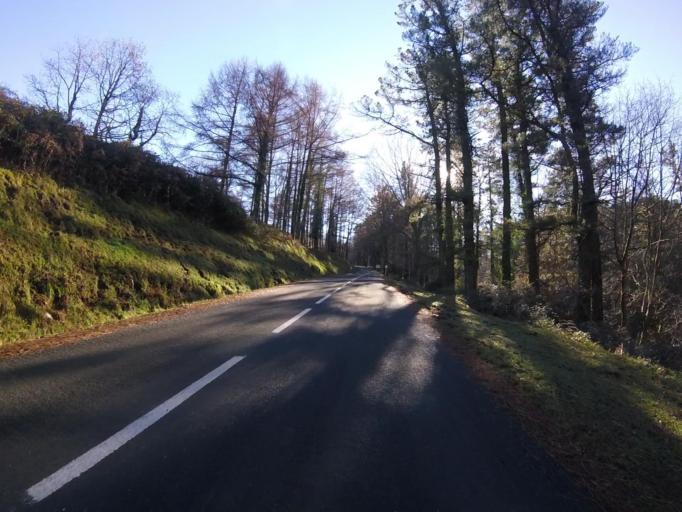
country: ES
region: Basque Country
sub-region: Provincia de Guipuzcoa
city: Irun
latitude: 43.3101
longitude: -1.7565
